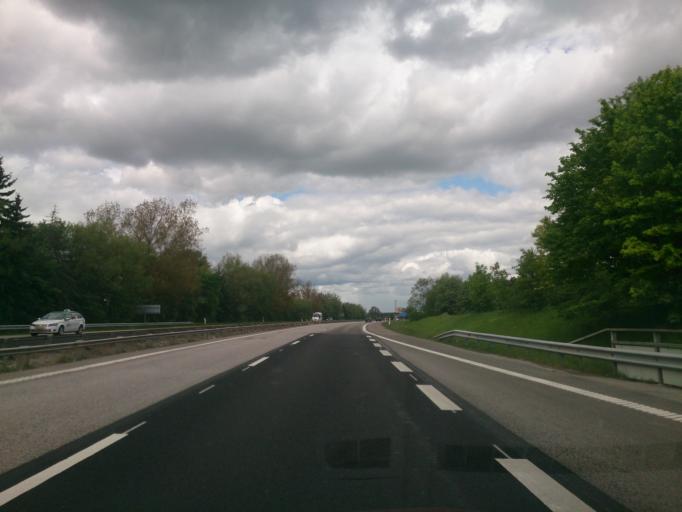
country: SE
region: OEstergoetland
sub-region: Norrkopings Kommun
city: Norrkoping
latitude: 58.5689
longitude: 16.2165
